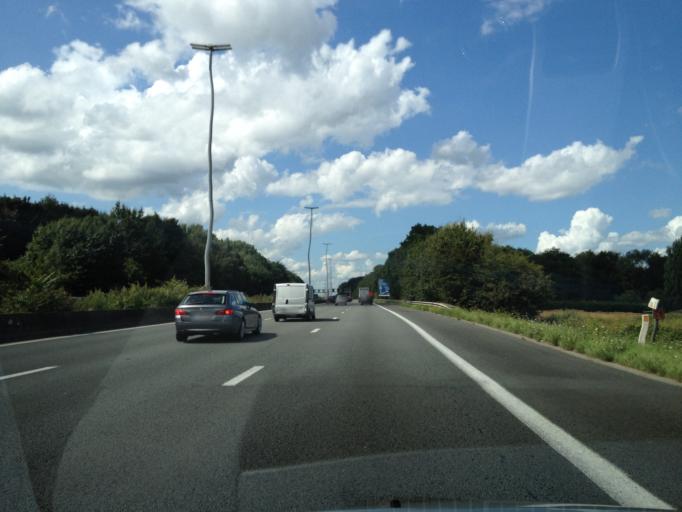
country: BE
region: Flanders
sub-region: Provincie Oost-Vlaanderen
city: Melle
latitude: 50.9946
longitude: 3.7869
